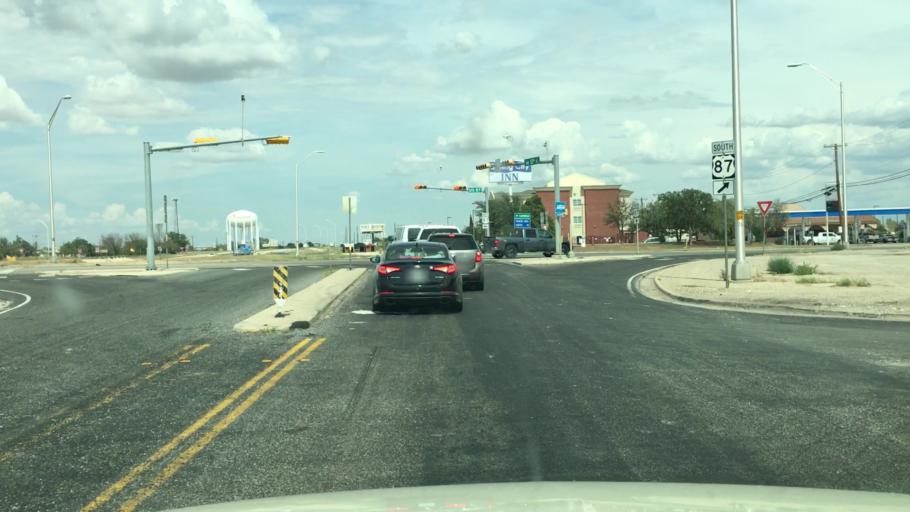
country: US
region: Texas
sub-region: Howard County
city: Big Spring
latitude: 32.2628
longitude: -101.4906
